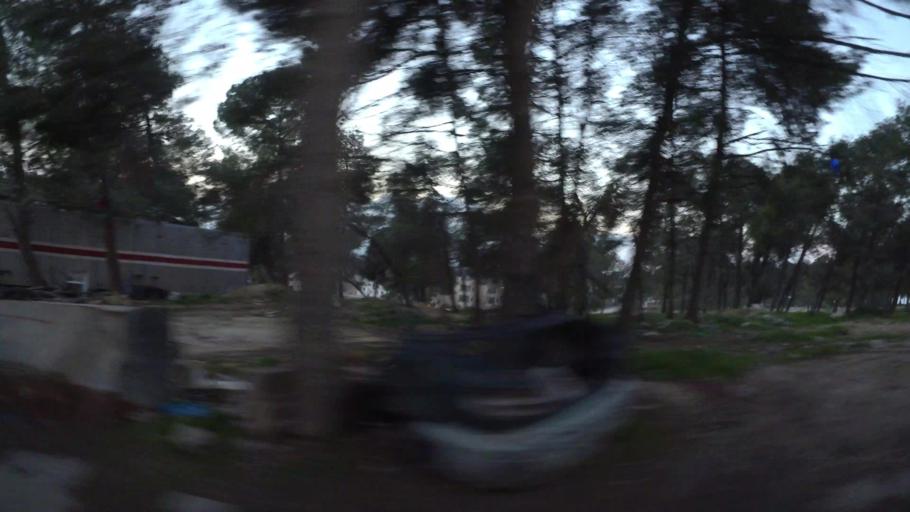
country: JO
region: Amman
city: Al Bunayyat ash Shamaliyah
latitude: 31.8901
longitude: 35.9207
